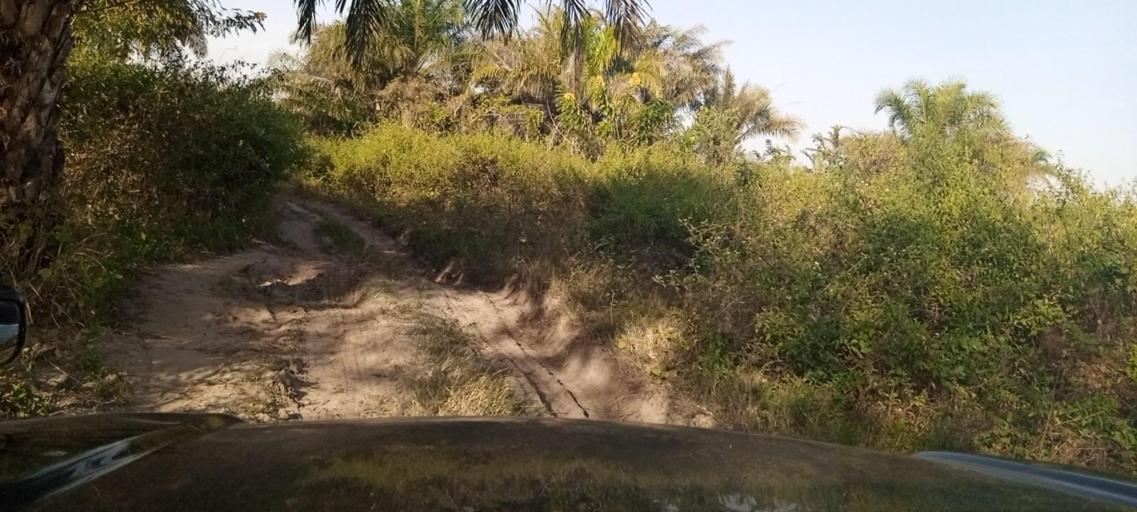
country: CD
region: Kasai-Oriental
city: Lubao
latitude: -5.4632
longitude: 25.6418
